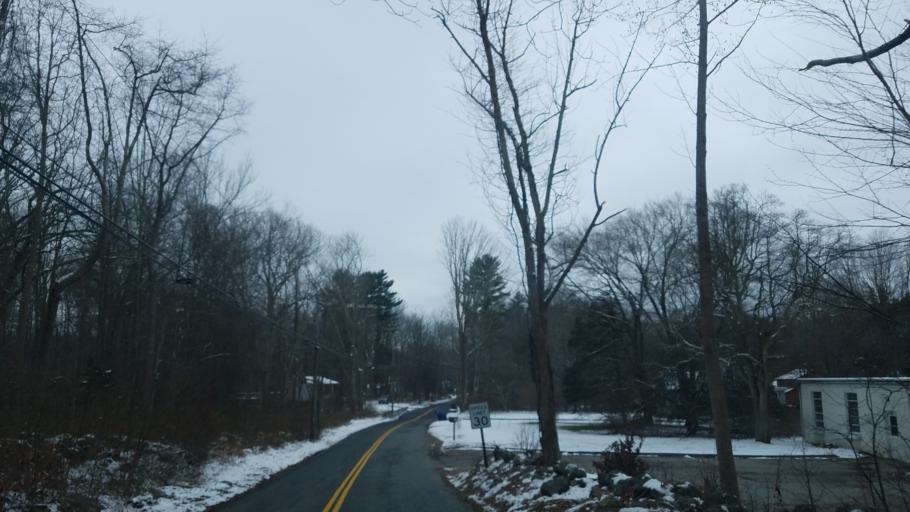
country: US
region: Connecticut
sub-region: New London County
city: Niantic
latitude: 41.3841
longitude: -72.1813
